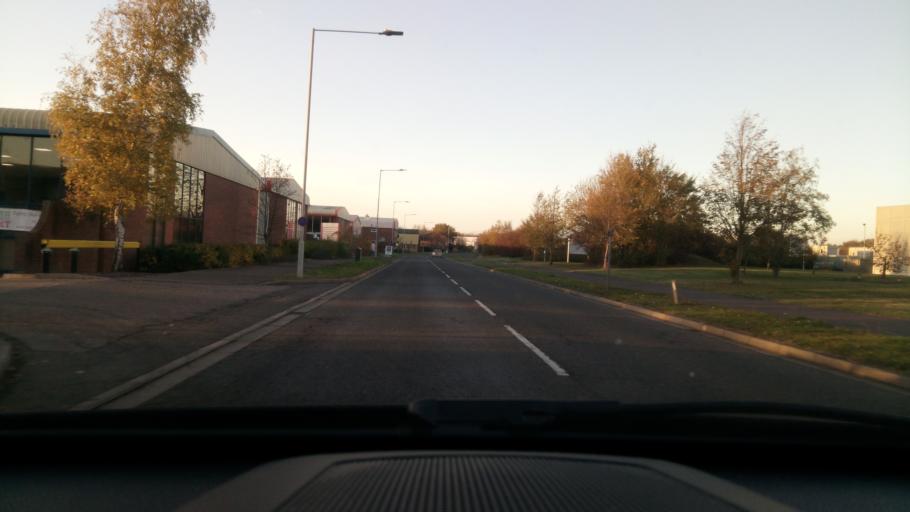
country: GB
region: England
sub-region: Peterborough
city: Marholm
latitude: 52.6150
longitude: -0.2887
